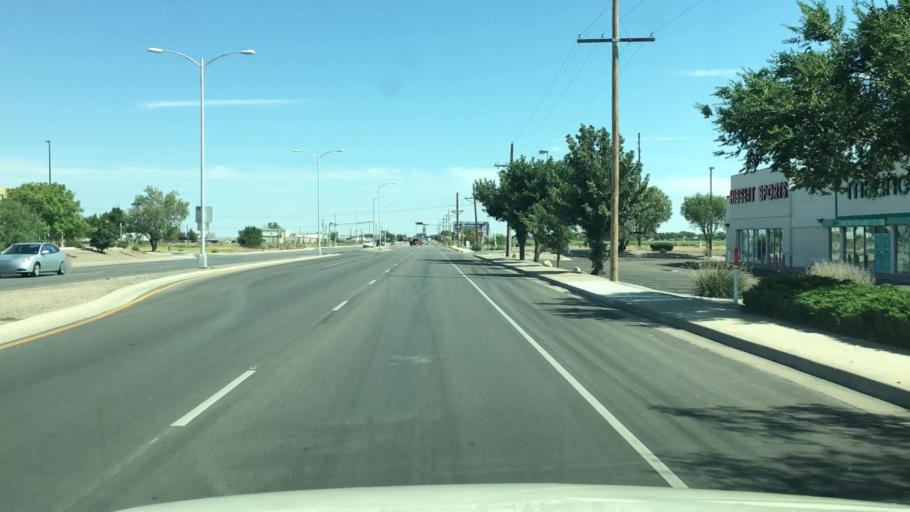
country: US
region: New Mexico
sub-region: Chaves County
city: Roswell
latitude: 33.4502
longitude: -104.5233
